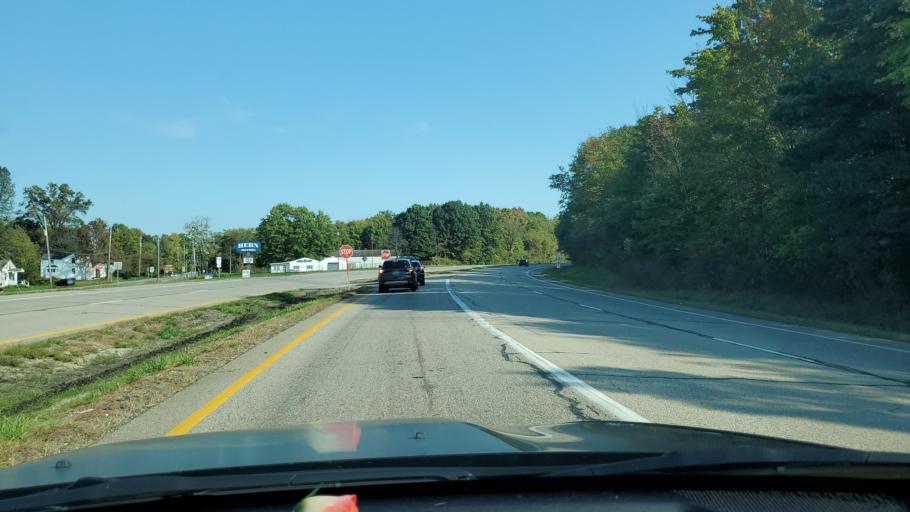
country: US
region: Ohio
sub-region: Trumbull County
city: Hubbard
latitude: 41.1866
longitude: -80.5680
